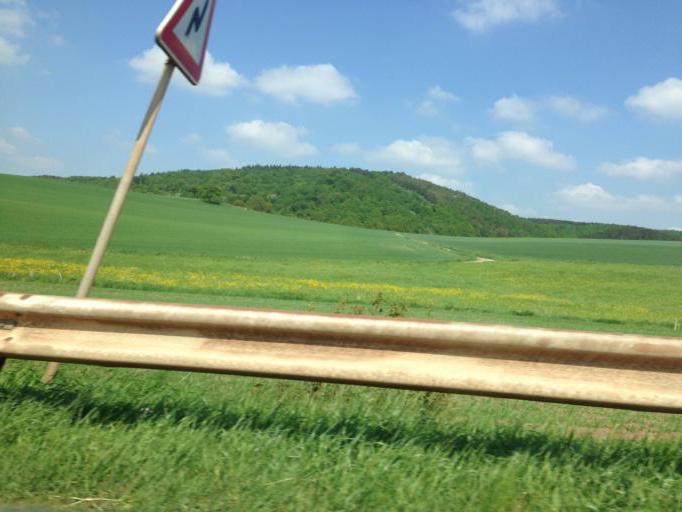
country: DE
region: North Rhine-Westphalia
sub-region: Regierungsbezirk Koln
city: Bad Munstereifel
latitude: 50.5527
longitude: 6.7215
